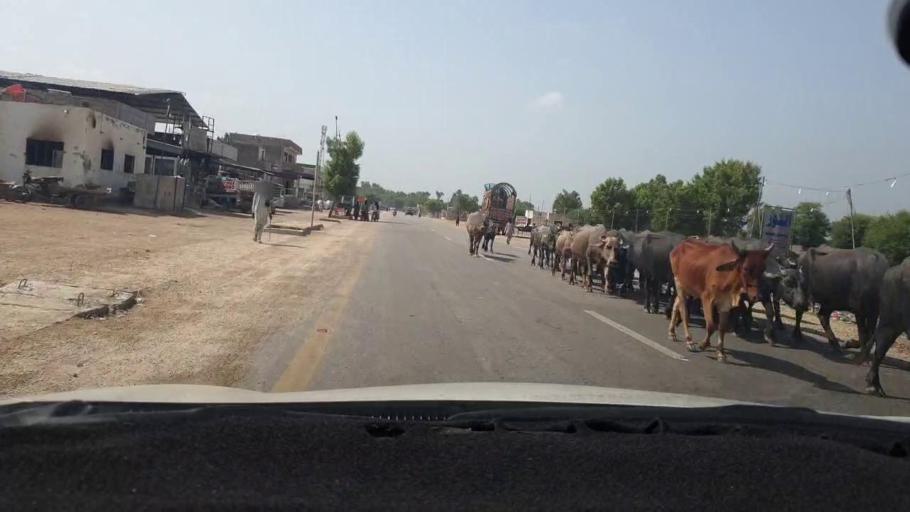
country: PK
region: Sindh
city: Mirpur Khas
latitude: 25.6664
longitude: 69.1033
